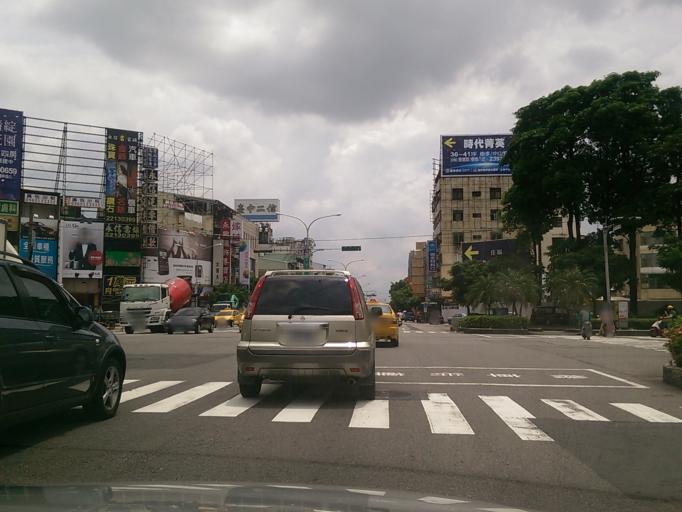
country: TW
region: Taiwan
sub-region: Taichung City
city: Taichung
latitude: 24.1483
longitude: 120.6943
